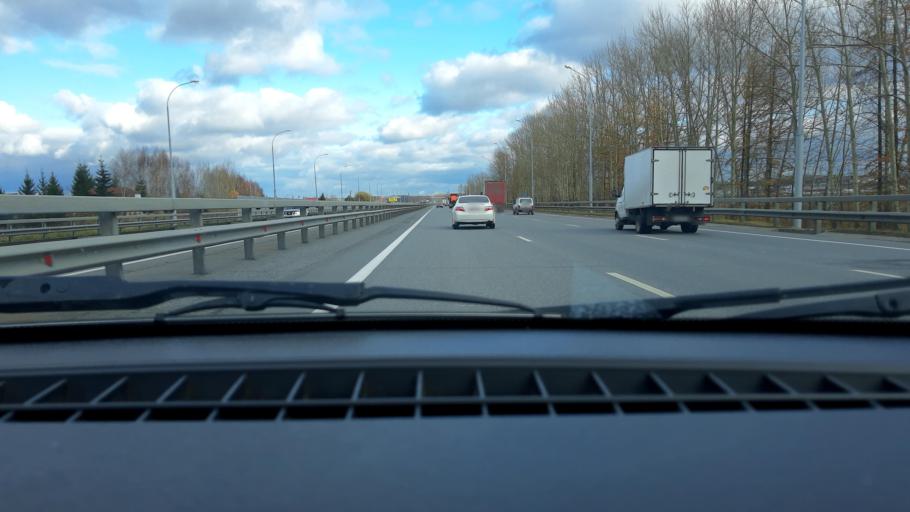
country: RU
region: Bashkortostan
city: Ufa
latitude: 54.6490
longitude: 56.0548
